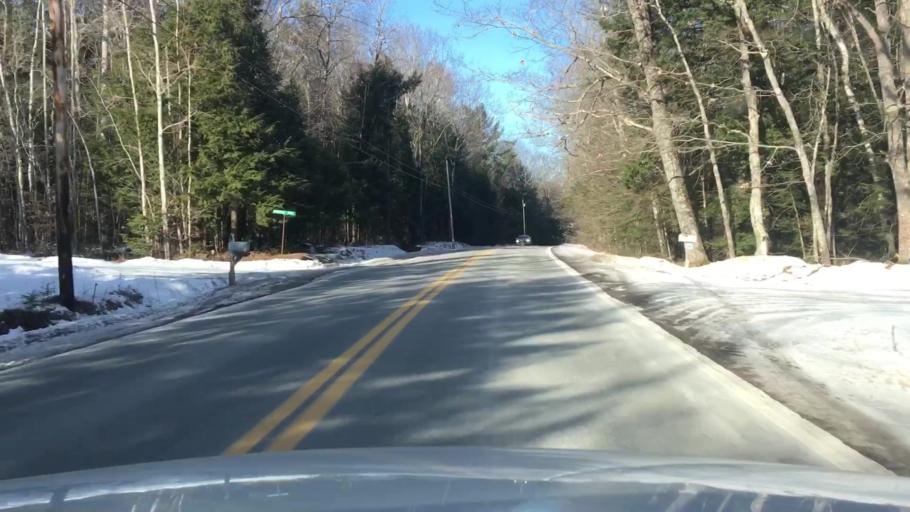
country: US
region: Maine
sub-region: Hancock County
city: Dedham
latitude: 44.6368
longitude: -68.6996
